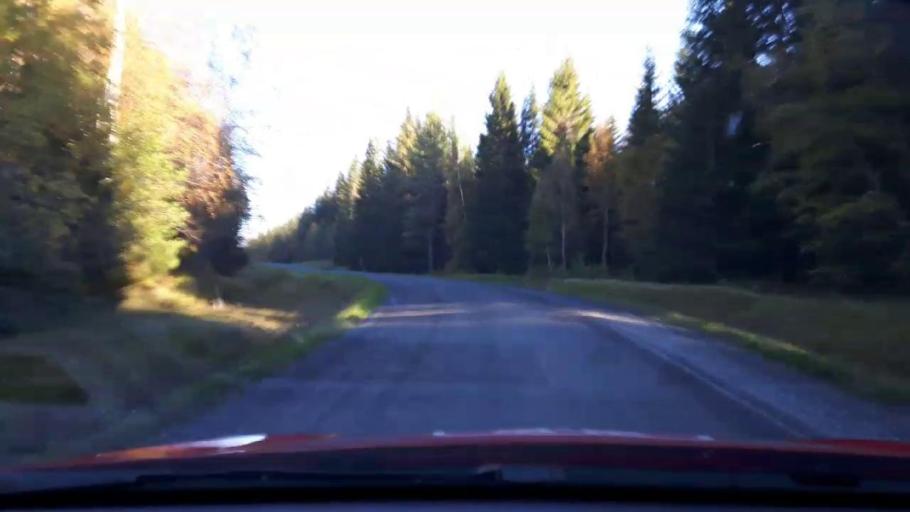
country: SE
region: Jaemtland
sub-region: OEstersunds Kommun
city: Lit
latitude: 63.6075
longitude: 14.7825
